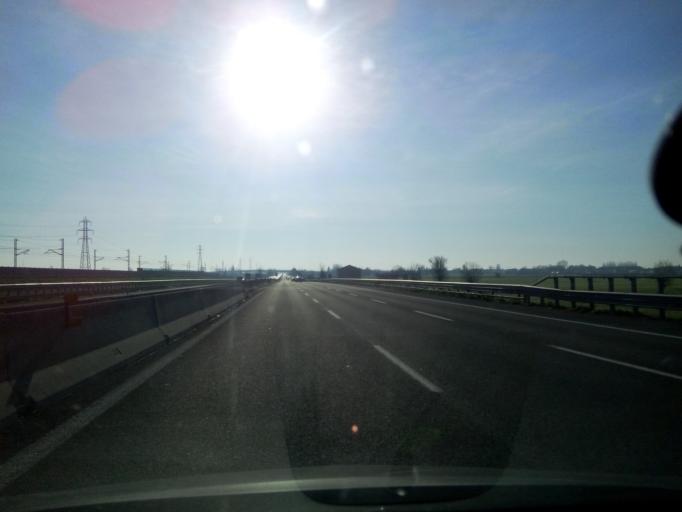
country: IT
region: Emilia-Romagna
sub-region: Provincia di Reggio Emilia
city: Massenzatico
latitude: 44.7193
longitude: 10.6761
